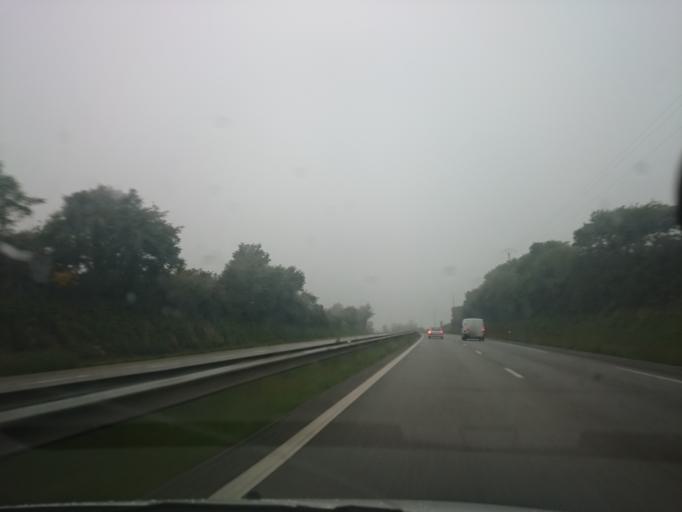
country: FR
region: Brittany
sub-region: Departement du Finistere
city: Briec
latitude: 48.1170
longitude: -4.0239
